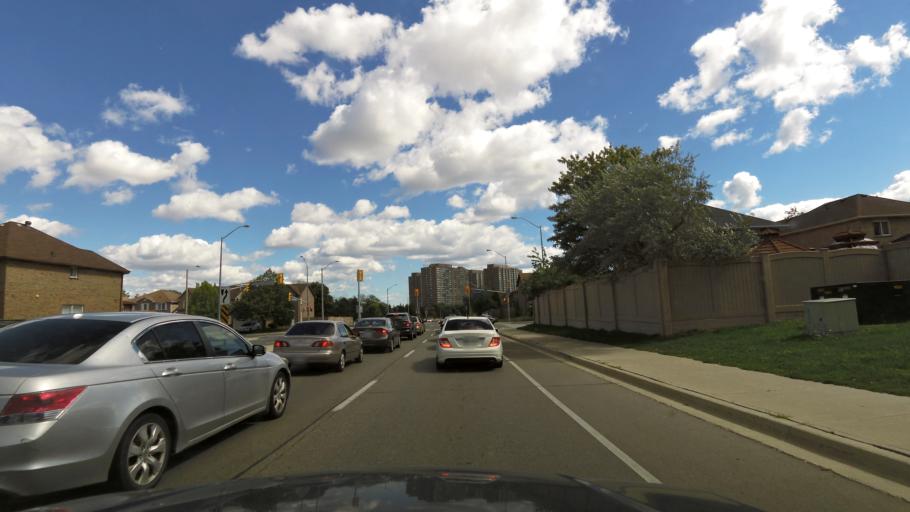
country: CA
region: Ontario
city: Mississauga
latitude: 43.5814
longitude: -79.6326
